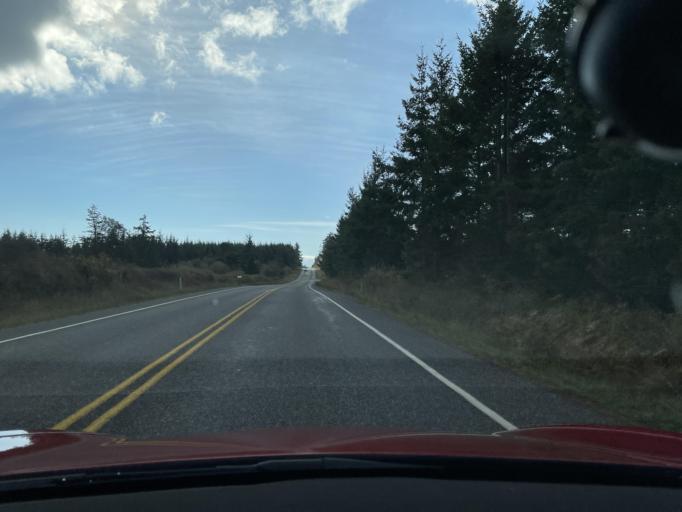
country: US
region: Washington
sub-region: San Juan County
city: Friday Harbor
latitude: 48.4835
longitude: -123.0317
